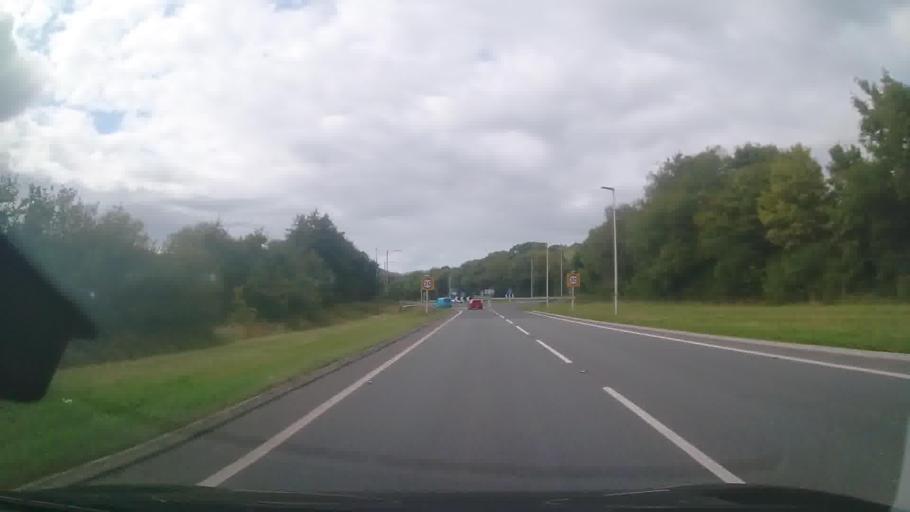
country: GB
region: Wales
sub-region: Gwynedd
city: Dolgellau
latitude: 52.7452
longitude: -3.8742
